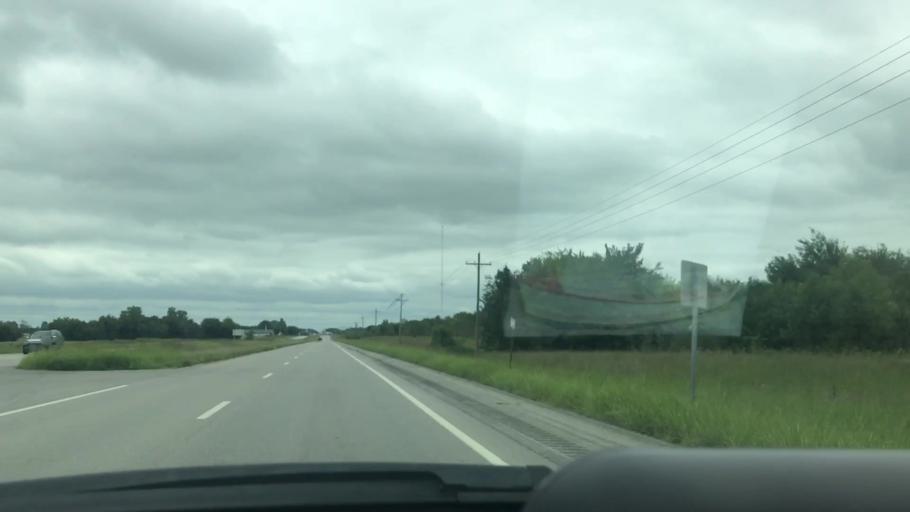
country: US
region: Oklahoma
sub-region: Mayes County
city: Pryor
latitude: 36.4158
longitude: -95.2794
